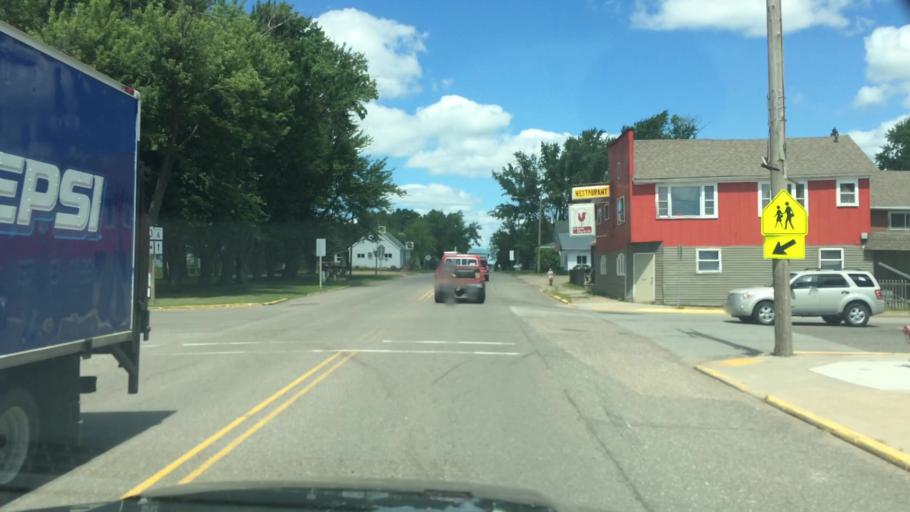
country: US
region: Wisconsin
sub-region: Taylor County
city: Medford
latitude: 45.0768
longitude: -90.3148
